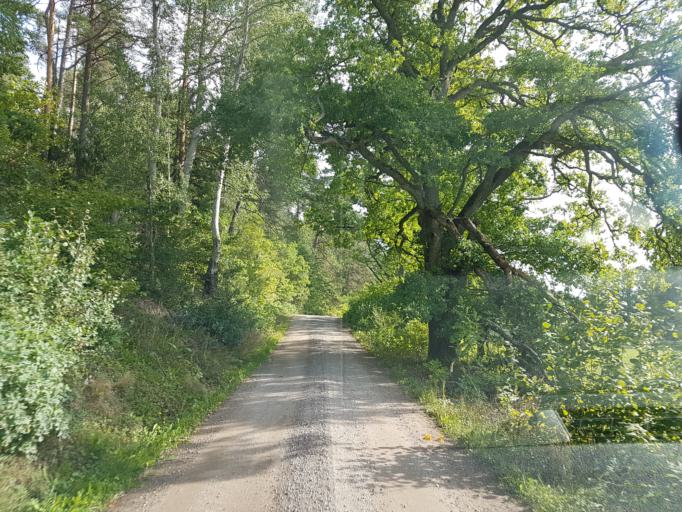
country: SE
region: OEstergoetland
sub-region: Linkopings Kommun
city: Sturefors
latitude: 58.3090
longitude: 15.8496
